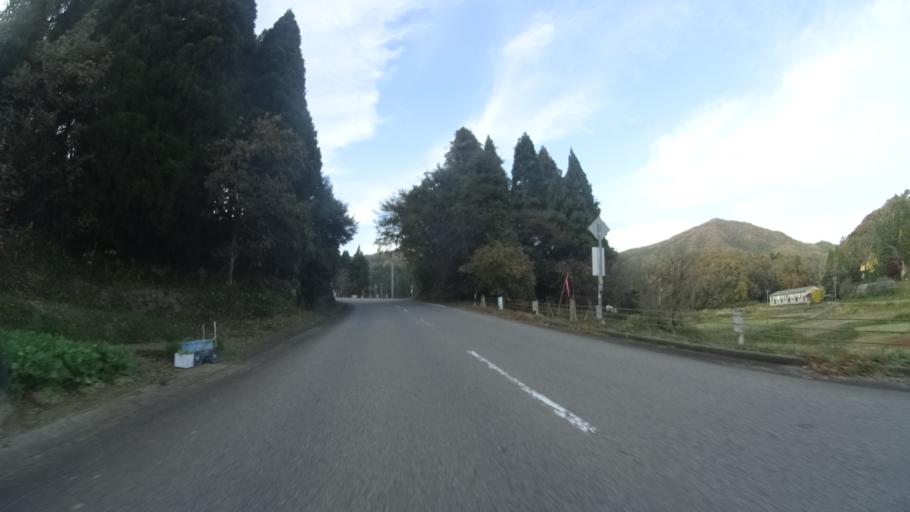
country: JP
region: Ishikawa
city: Nanao
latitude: 37.1960
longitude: 136.7140
